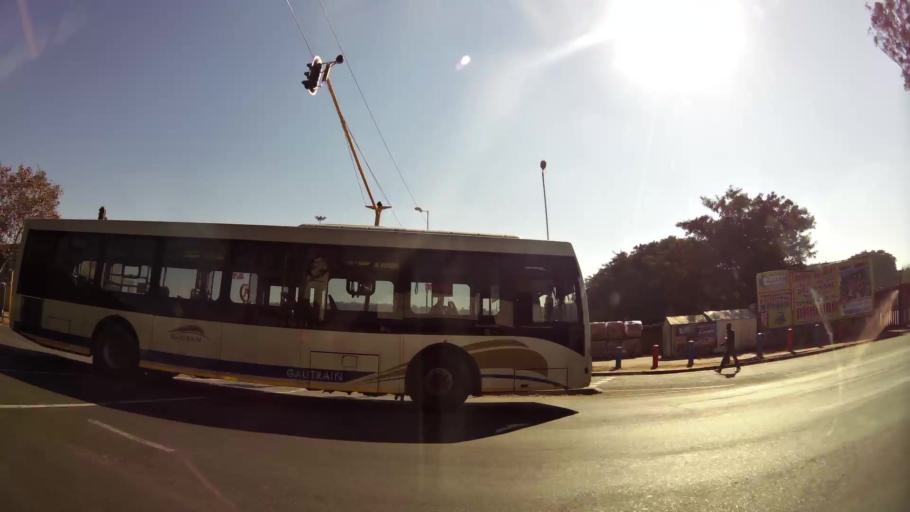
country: ZA
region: Gauteng
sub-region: City of Tshwane Metropolitan Municipality
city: Pretoria
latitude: -25.7393
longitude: 28.1851
